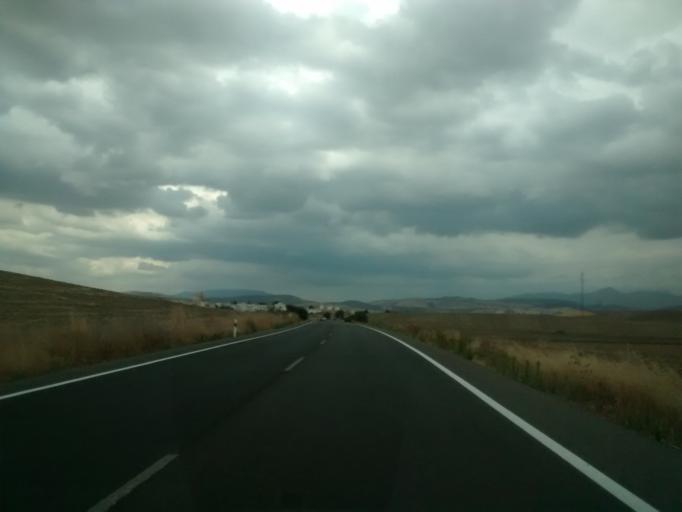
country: ES
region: Andalusia
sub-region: Provincia de Cadiz
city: Villamartin
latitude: 36.8530
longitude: -5.6478
